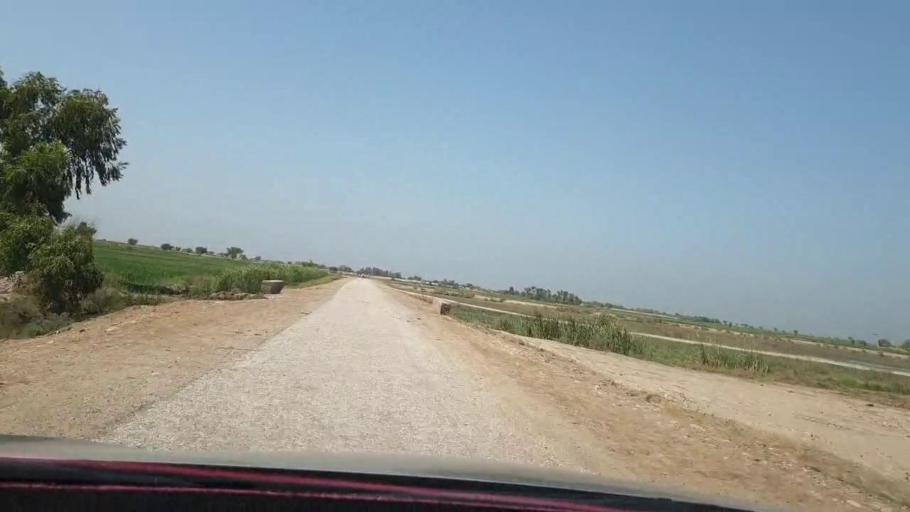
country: PK
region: Sindh
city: Warah
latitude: 27.5459
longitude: 67.7426
